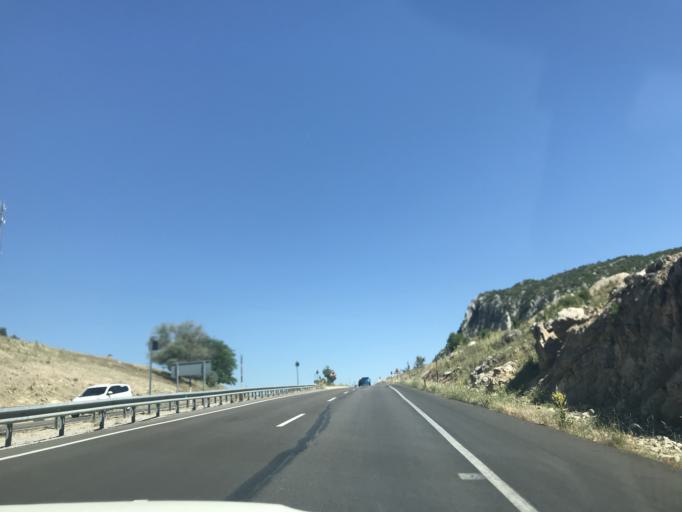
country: TR
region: Antalya
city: Dagbeli
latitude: 37.1677
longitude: 30.4988
